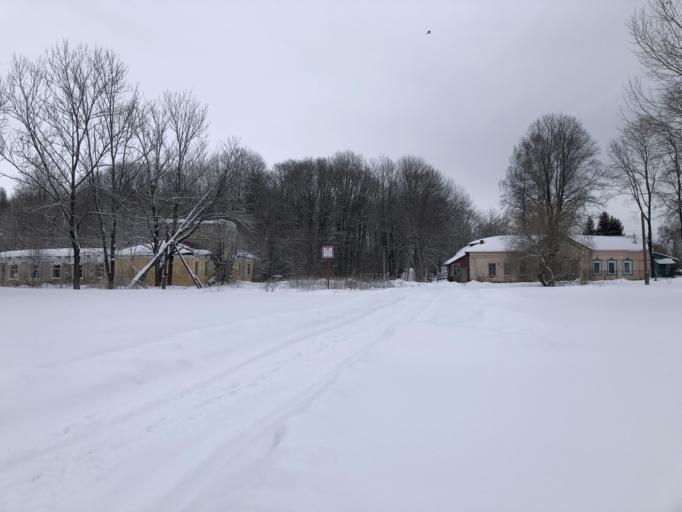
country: RU
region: Smolensk
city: Shatalovo
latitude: 54.3374
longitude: 32.5556
